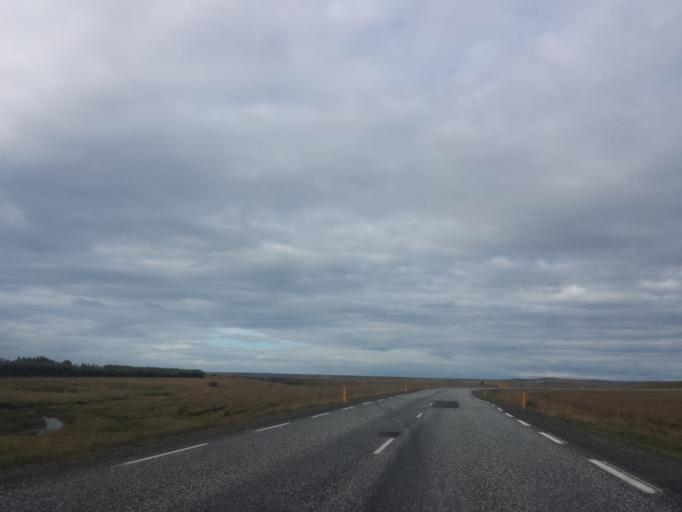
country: IS
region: West
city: Borgarnes
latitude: 64.3745
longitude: -21.8438
